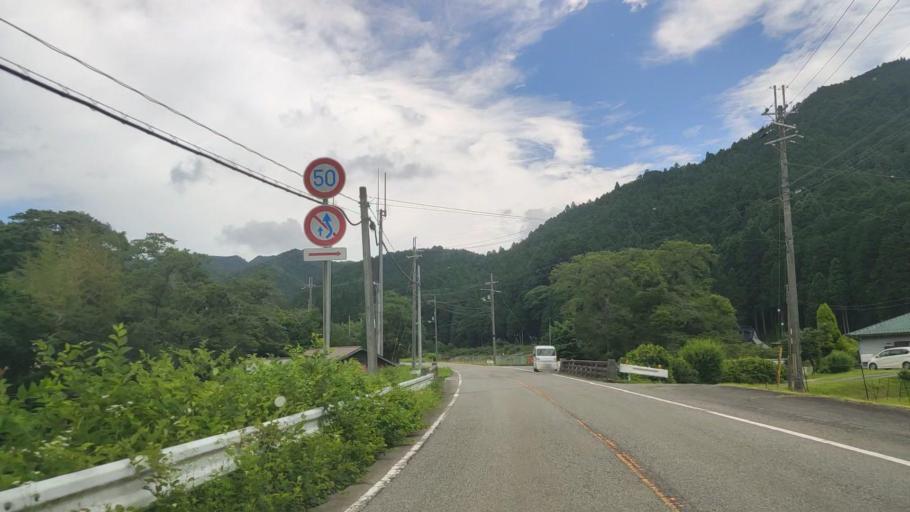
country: JP
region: Kyoto
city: Fukuchiyama
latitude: 35.2008
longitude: 134.9375
